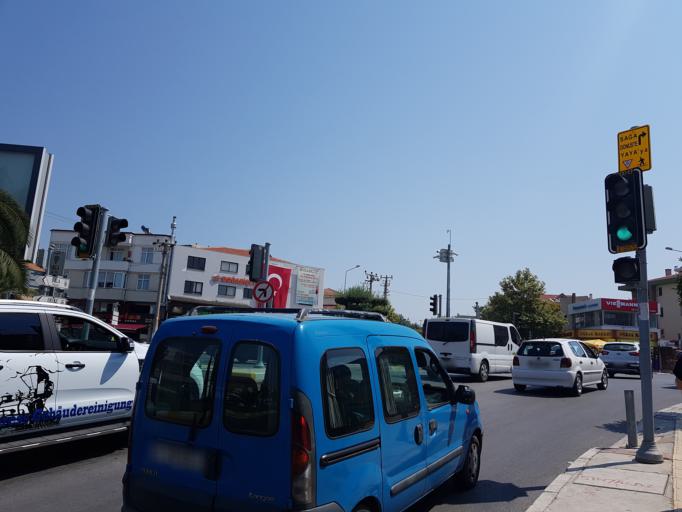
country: TR
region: Izmir
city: Urla
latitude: 38.3279
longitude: 26.7660
